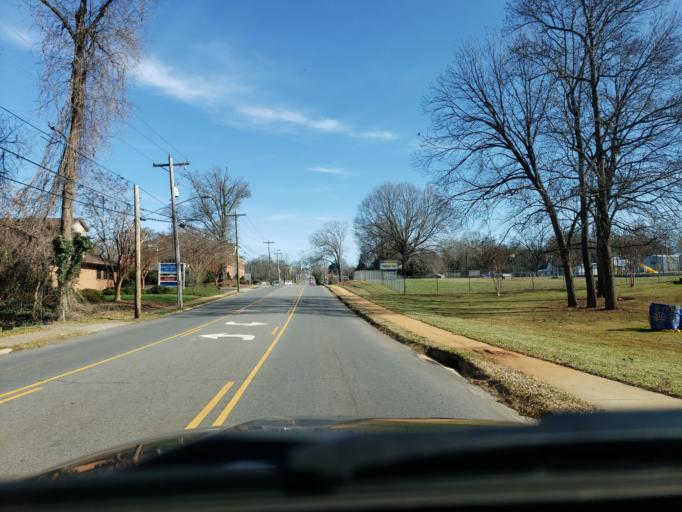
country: US
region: North Carolina
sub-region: Cleveland County
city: Kings Mountain
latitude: 35.2409
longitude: -81.3528
